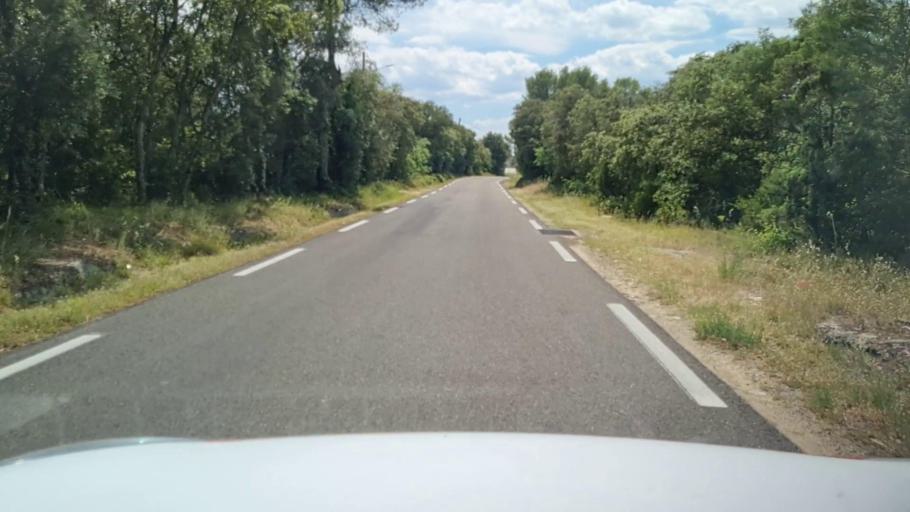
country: FR
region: Languedoc-Roussillon
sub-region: Departement du Gard
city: Villevieille
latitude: 43.8047
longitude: 4.1104
